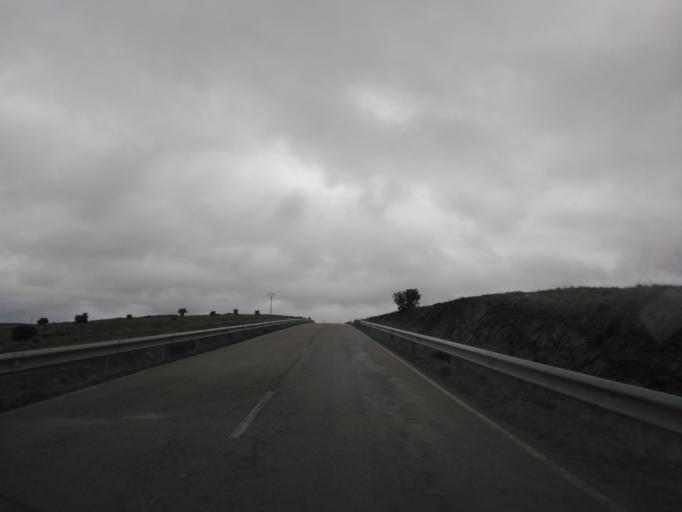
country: ES
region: Castille and Leon
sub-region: Provincia de Salamanca
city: Doninos de Salamanca
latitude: 40.9697
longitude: -5.7123
